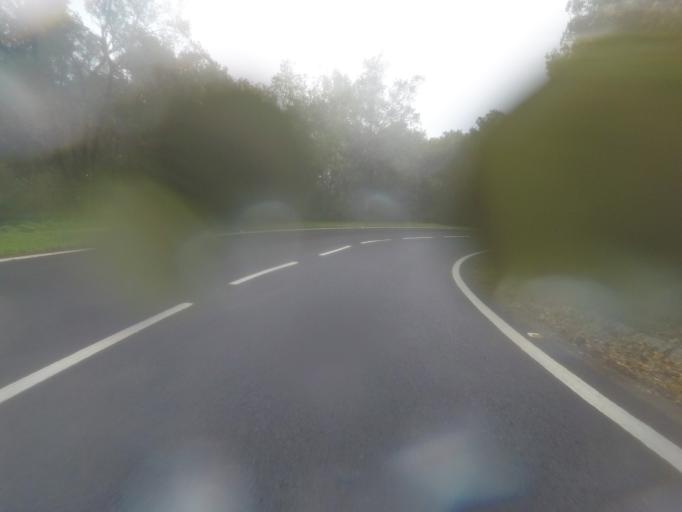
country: ES
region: Canary Islands
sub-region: Provincia de Santa Cruz de Tenerife
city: Vallehermosa
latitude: 28.1406
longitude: -17.2836
